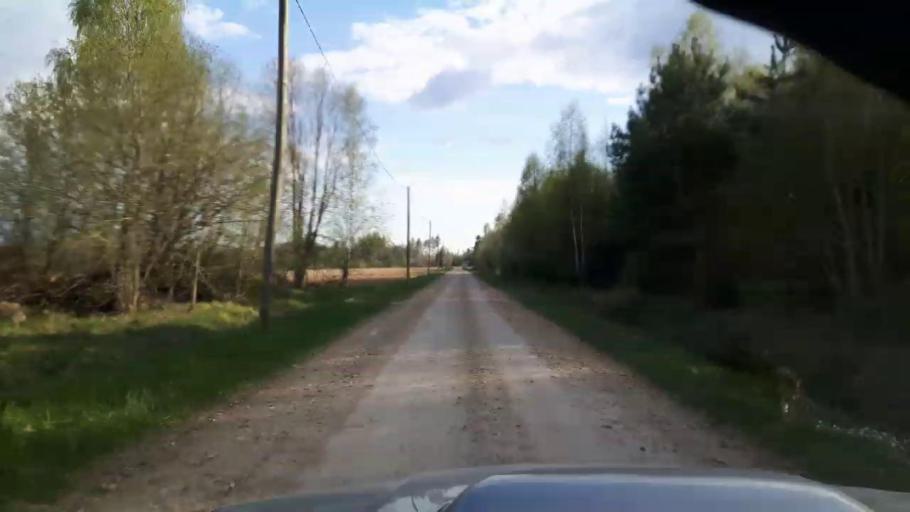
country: EE
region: Paernumaa
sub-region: Sindi linn
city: Sindi
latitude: 58.4341
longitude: 24.8070
